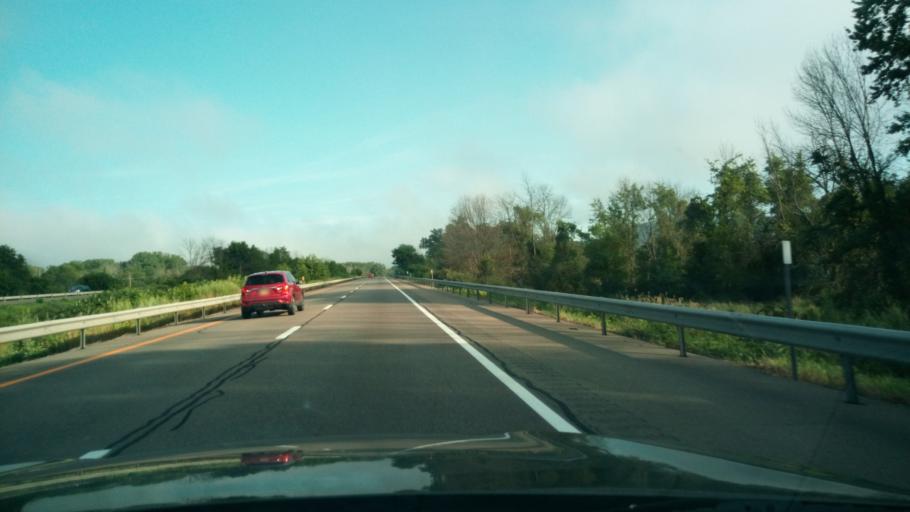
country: US
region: New York
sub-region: Steuben County
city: Bath
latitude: 42.2677
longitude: -77.2188
